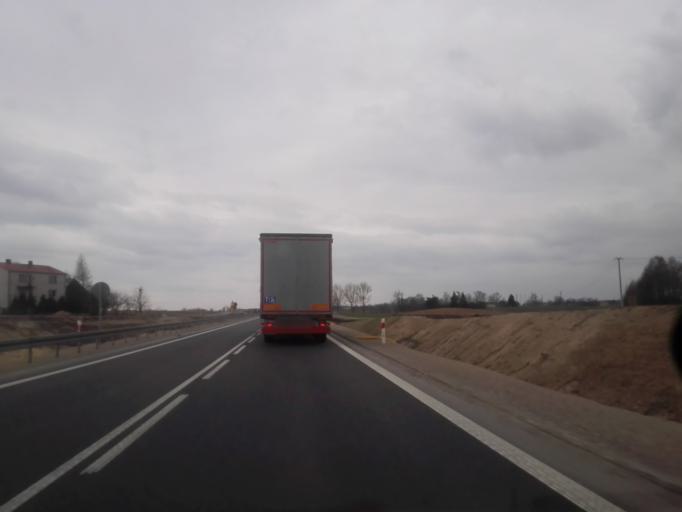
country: PL
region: Podlasie
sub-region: Powiat augustowski
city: Augustow
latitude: 53.7837
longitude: 22.8470
